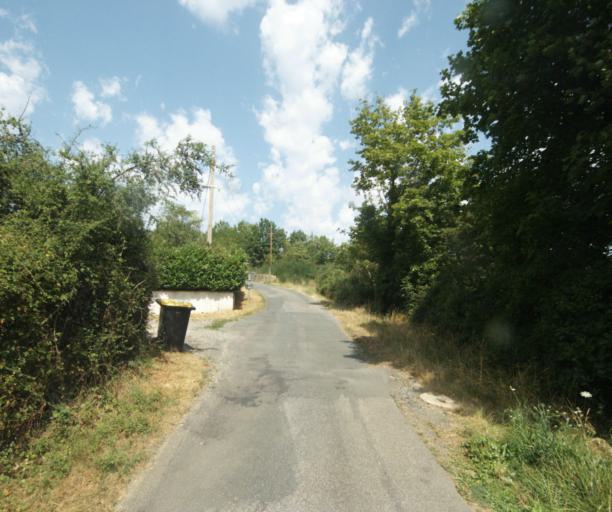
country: FR
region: Rhone-Alpes
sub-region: Departement du Rhone
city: Lentilly
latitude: 45.8324
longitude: 4.6628
